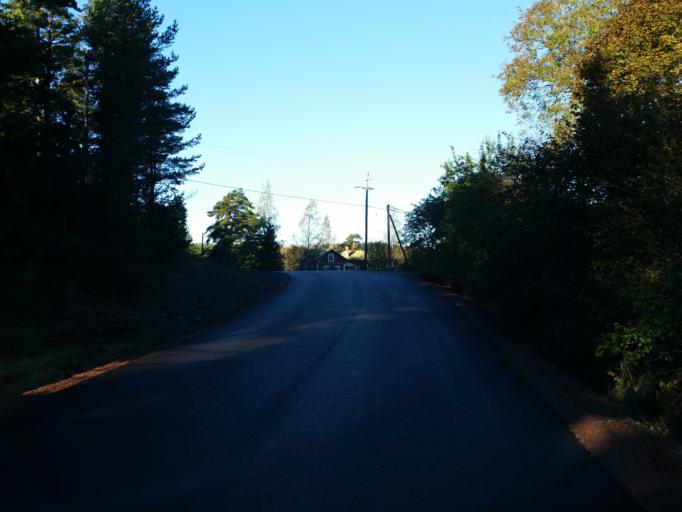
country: AX
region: Alands landsbygd
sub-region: Sund
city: Sund
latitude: 60.2298
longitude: 20.0897
